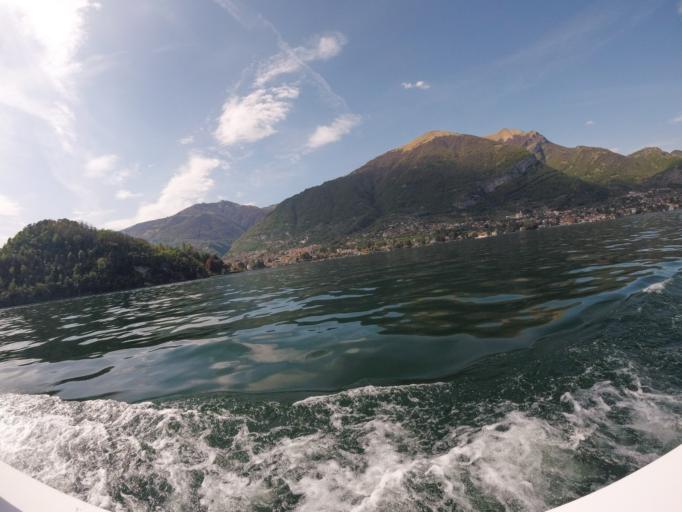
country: IT
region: Lombardy
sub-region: Provincia di Como
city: Mezzegra
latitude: 45.9681
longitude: 9.2083
